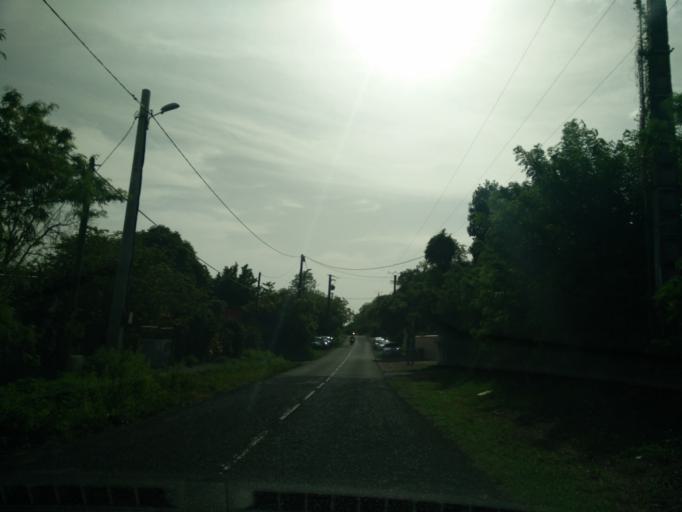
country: MQ
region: Martinique
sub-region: Martinique
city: Saint-Pierre
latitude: 14.7816
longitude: -61.2081
